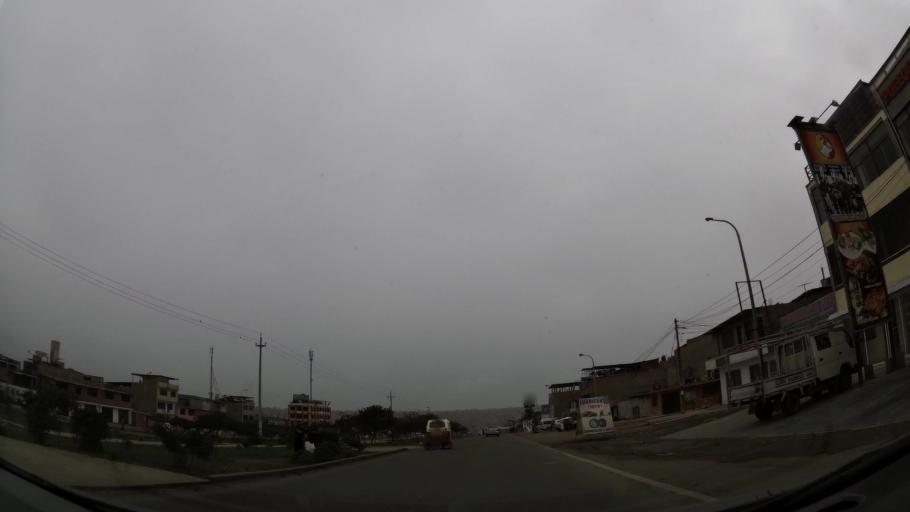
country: PE
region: Lima
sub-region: Lima
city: Surco
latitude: -12.2230
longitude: -76.9361
